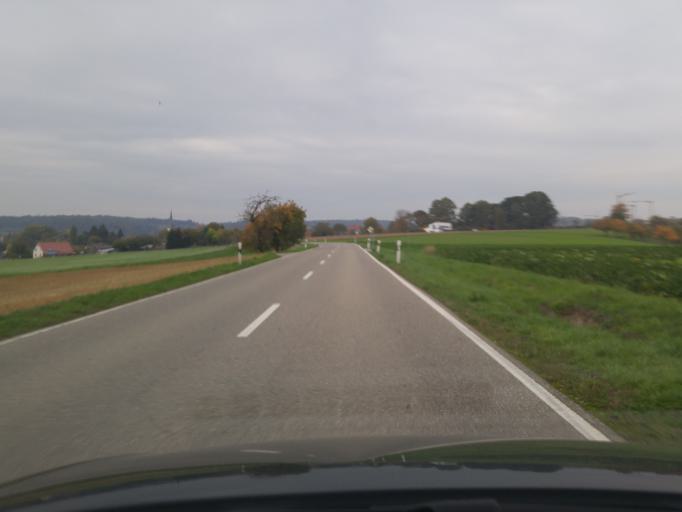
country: DE
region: Baden-Wuerttemberg
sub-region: Regierungsbezirk Stuttgart
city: Bretzfeld
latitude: 49.1677
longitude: 9.4140
